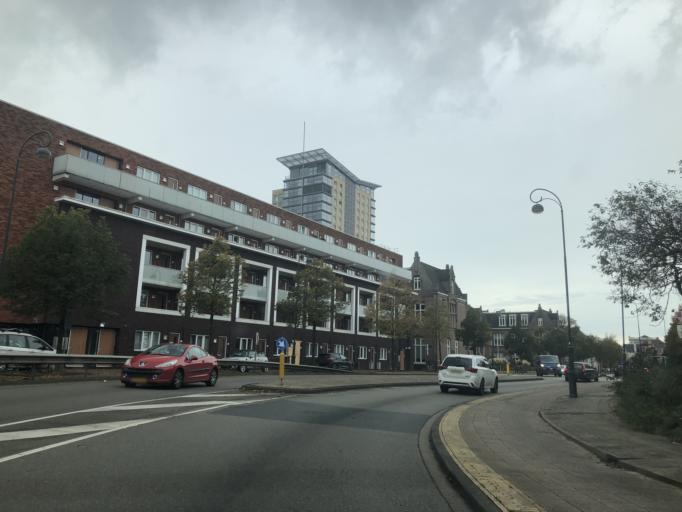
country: NL
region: North Holland
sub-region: Gemeente Haarlem
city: Haarlem
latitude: 52.3708
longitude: 4.6366
